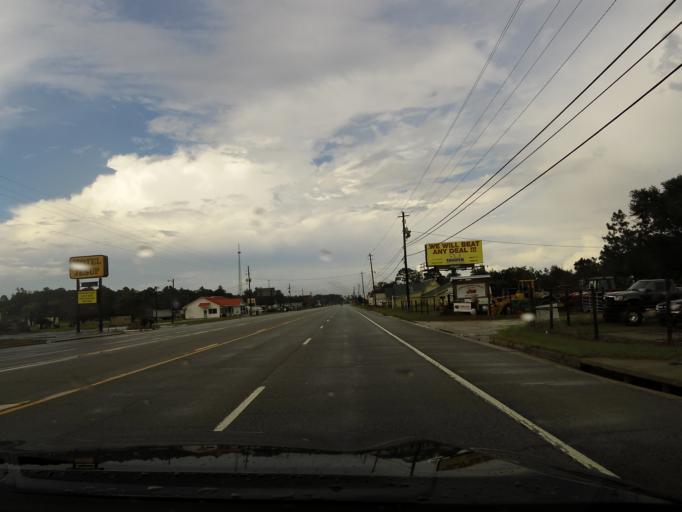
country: US
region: Georgia
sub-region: Wayne County
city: Jesup
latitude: 31.6536
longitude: -81.8524
